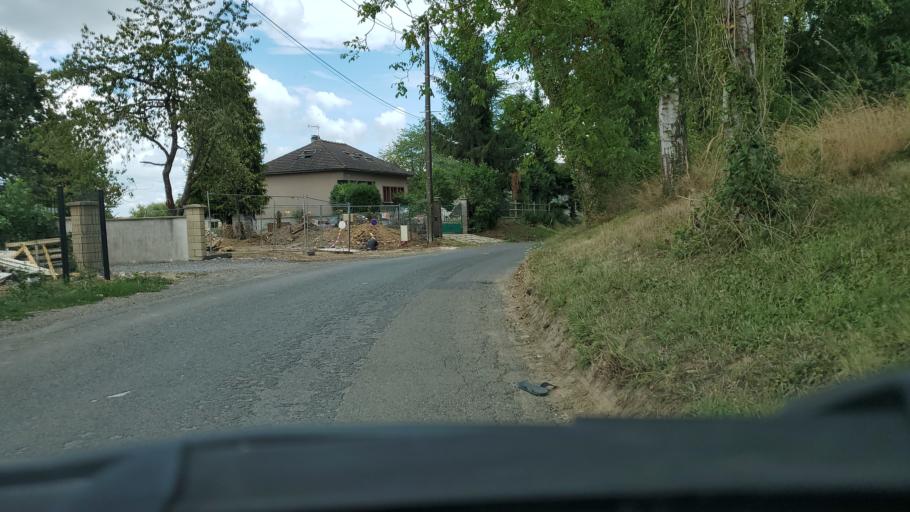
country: FR
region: Ile-de-France
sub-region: Departement de Seine-et-Marne
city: Mouroux
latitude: 48.8418
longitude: 3.0274
